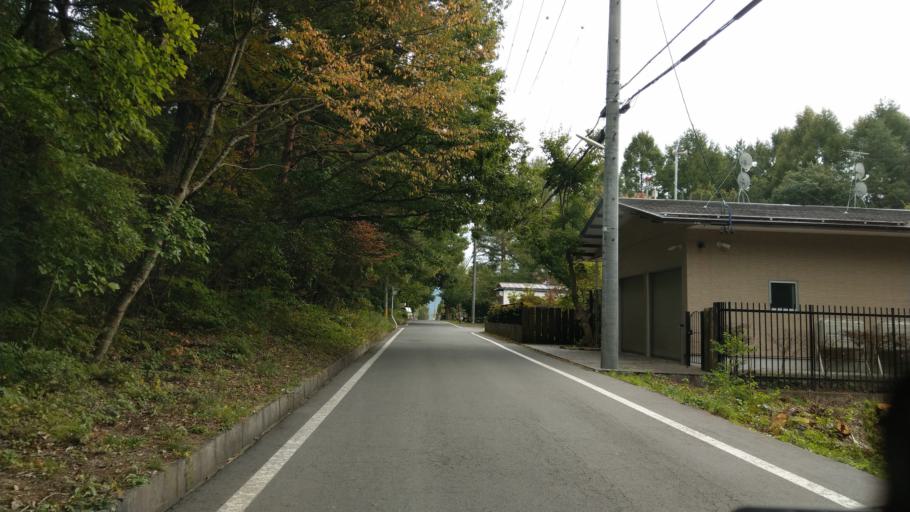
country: JP
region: Nagano
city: Komoro
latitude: 36.3259
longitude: 138.5263
